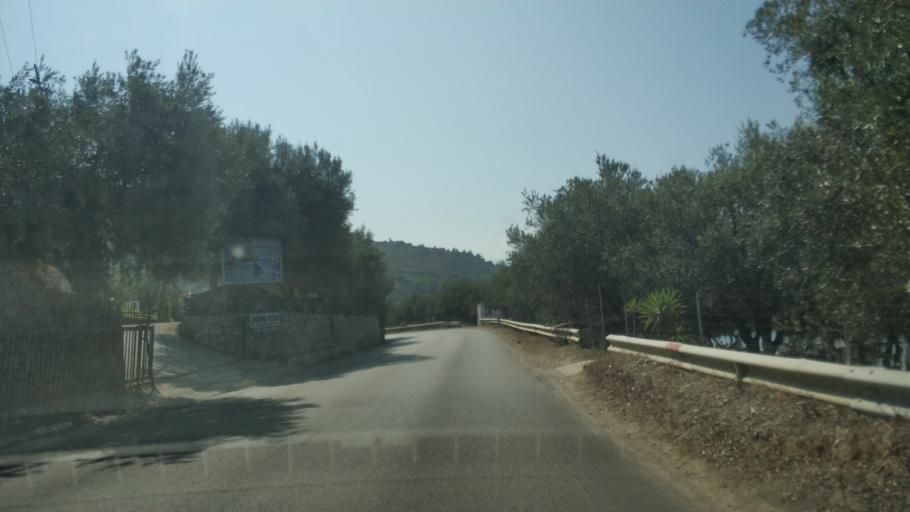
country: AL
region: Vlore
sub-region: Rrethi i Vlores
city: Orikum
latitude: 40.3874
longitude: 19.4836
